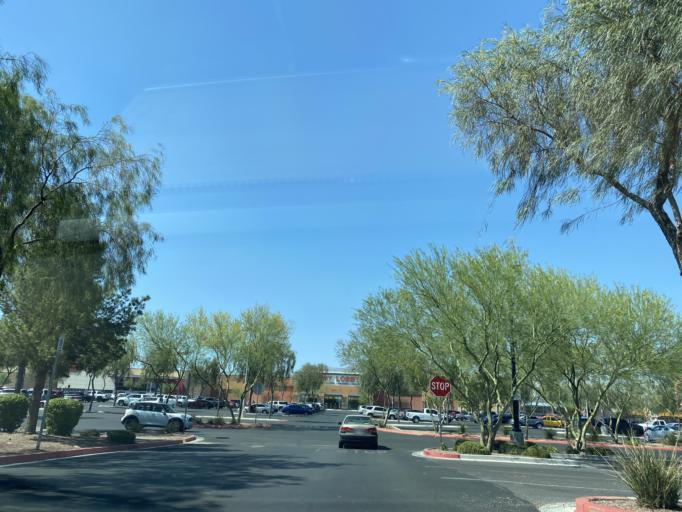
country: US
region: Nevada
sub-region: Clark County
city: North Las Vegas
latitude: 36.2715
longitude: -115.2089
